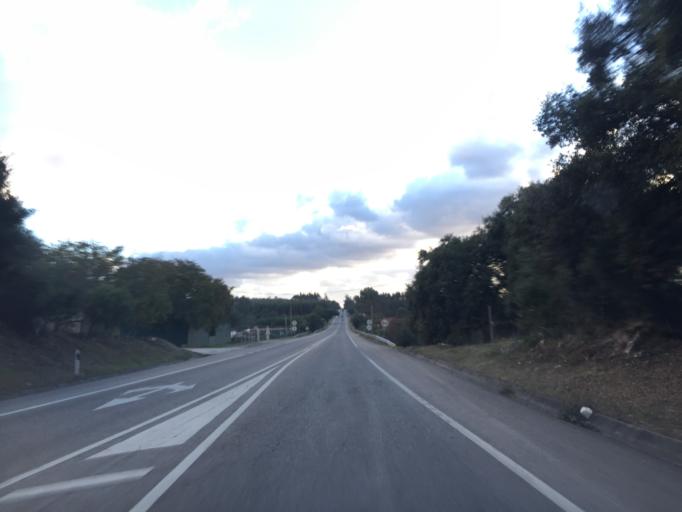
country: PT
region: Leiria
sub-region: Alcobaca
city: Turquel
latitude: 39.4802
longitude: -8.9370
